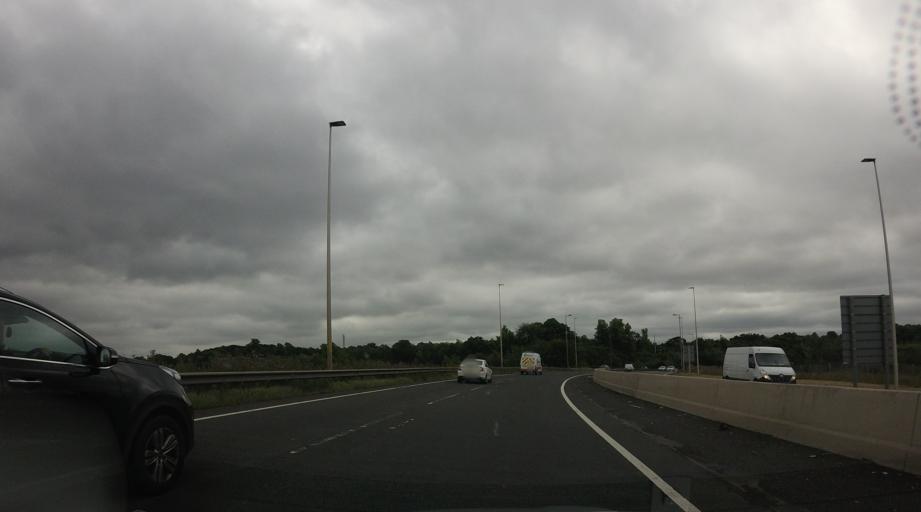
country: GB
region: Scotland
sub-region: South Lanarkshire
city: Bothwell
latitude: 55.7979
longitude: -4.0552
